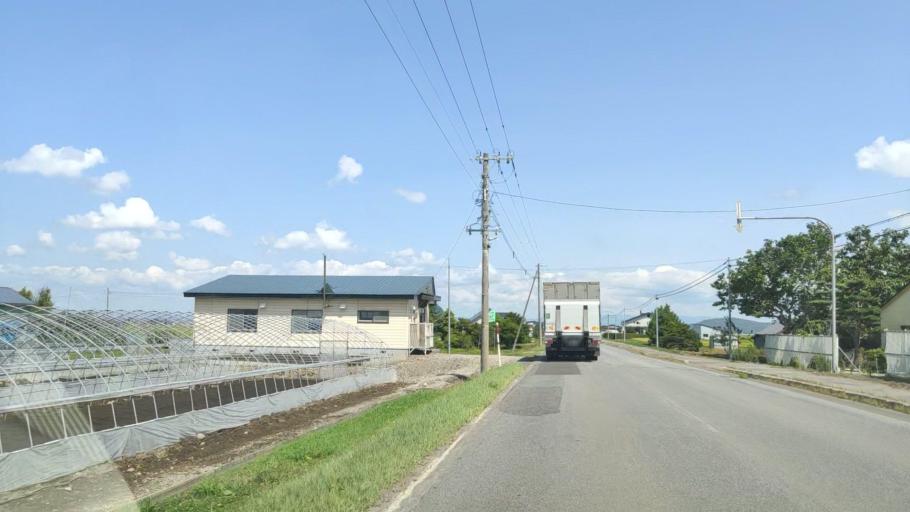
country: JP
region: Hokkaido
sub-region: Asahikawa-shi
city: Asahikawa
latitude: 43.7177
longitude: 142.4575
